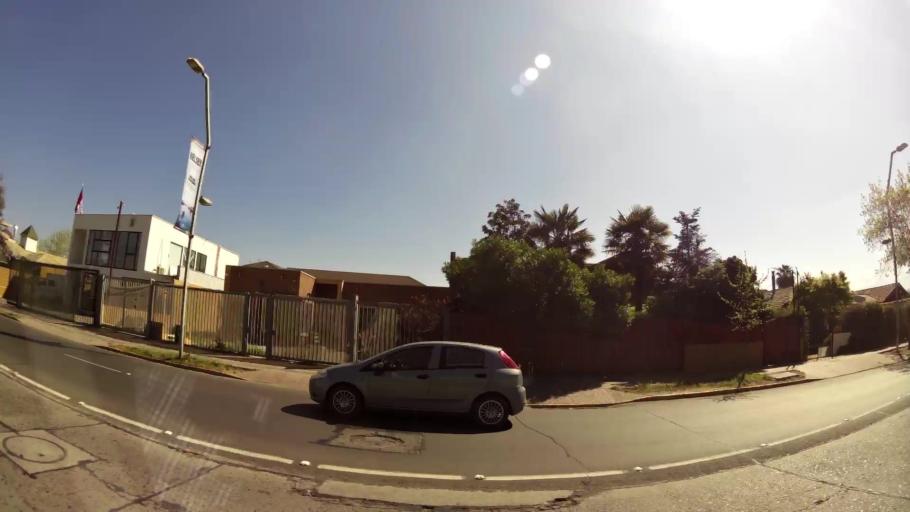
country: CL
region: Santiago Metropolitan
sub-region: Provincia de Santiago
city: Villa Presidente Frei, Nunoa, Santiago, Chile
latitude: -33.4179
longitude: -70.5508
